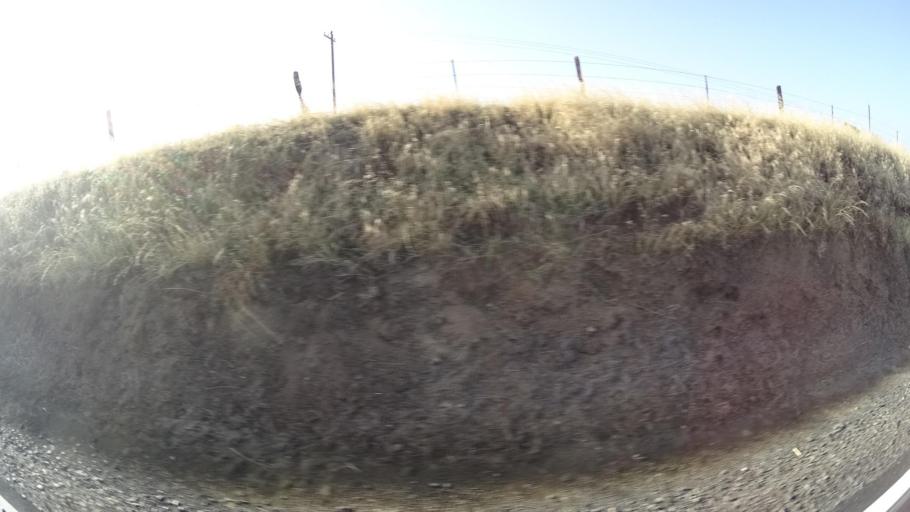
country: US
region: California
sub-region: Tulare County
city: Richgrove
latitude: 35.7525
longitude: -119.0090
